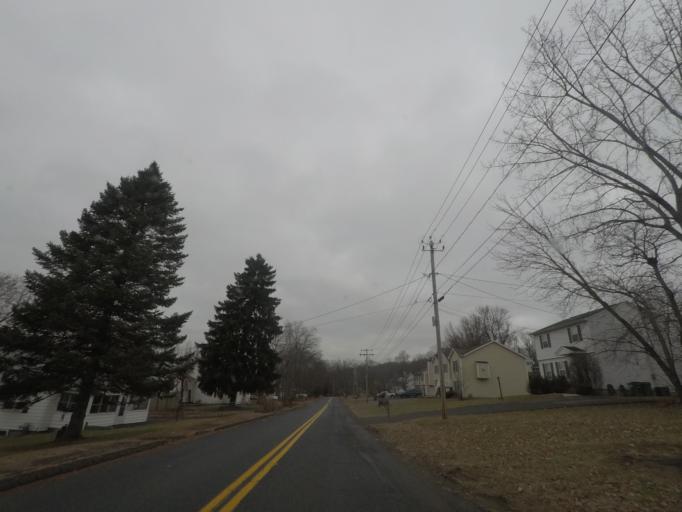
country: US
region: New York
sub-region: Saratoga County
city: Waterford
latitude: 42.7980
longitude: -73.6610
